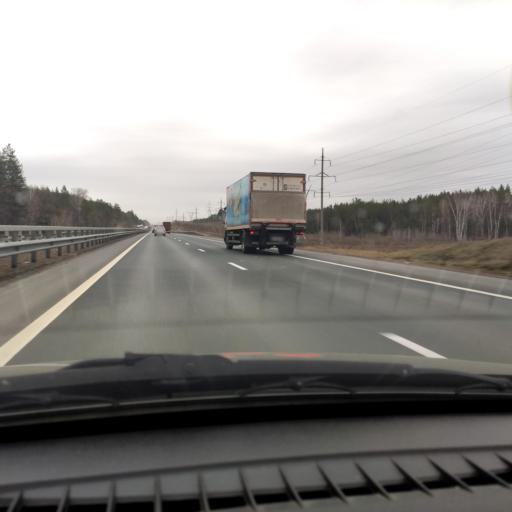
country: RU
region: Samara
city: Povolzhskiy
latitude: 53.5167
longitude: 49.7332
